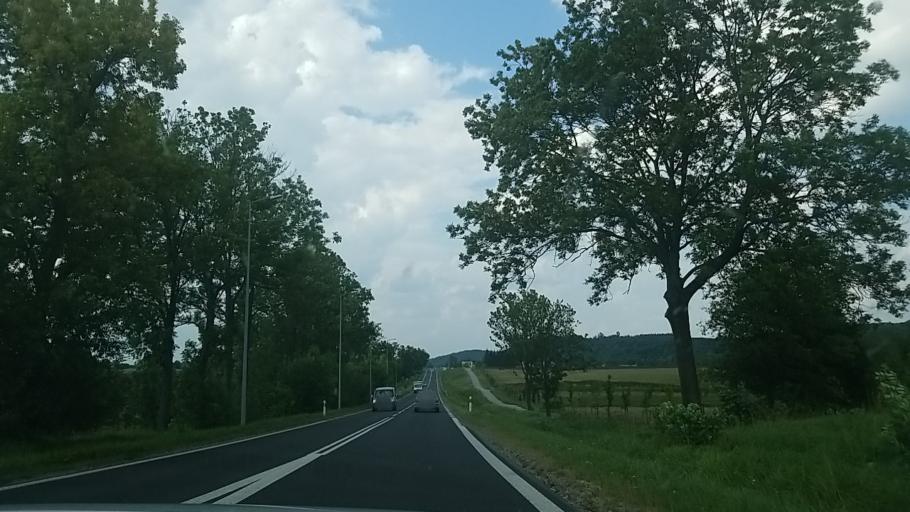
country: PL
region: Lublin Voivodeship
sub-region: Powiat bilgorajski
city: Goraj
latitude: 50.7324
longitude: 22.6676
